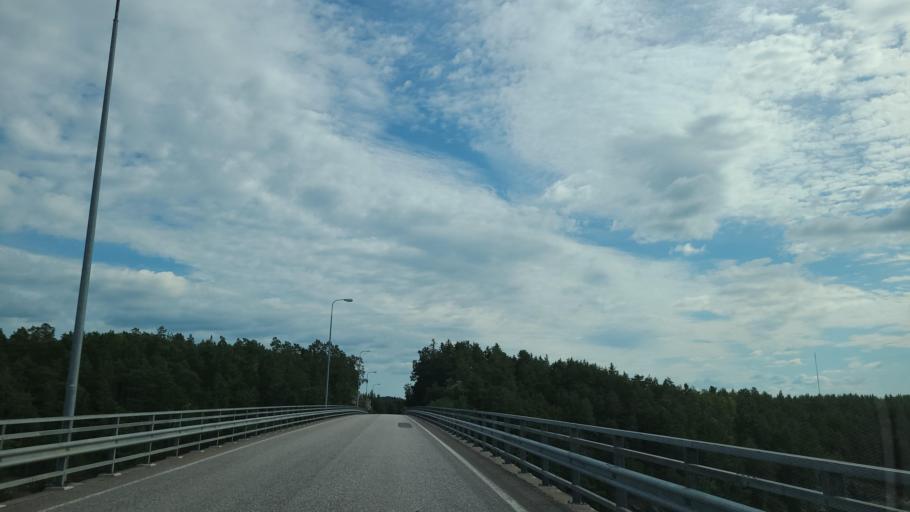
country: FI
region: Varsinais-Suomi
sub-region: Turku
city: Rymaettylae
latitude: 60.3372
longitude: 21.9794
